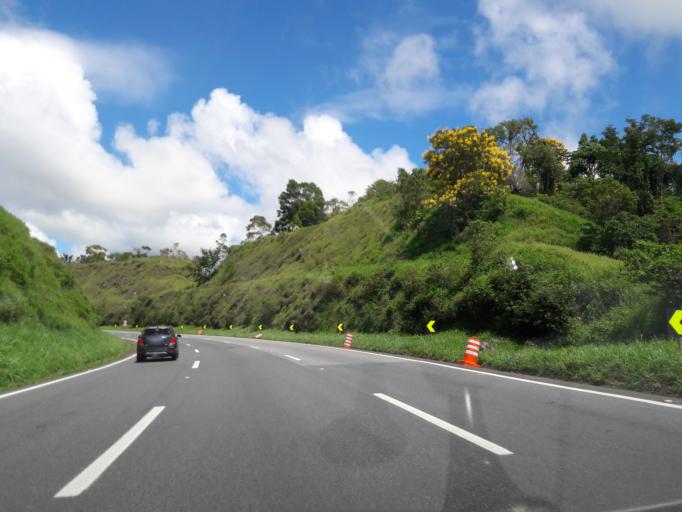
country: BR
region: Sao Paulo
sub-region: Cajati
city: Cajati
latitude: -24.9562
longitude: -48.4628
